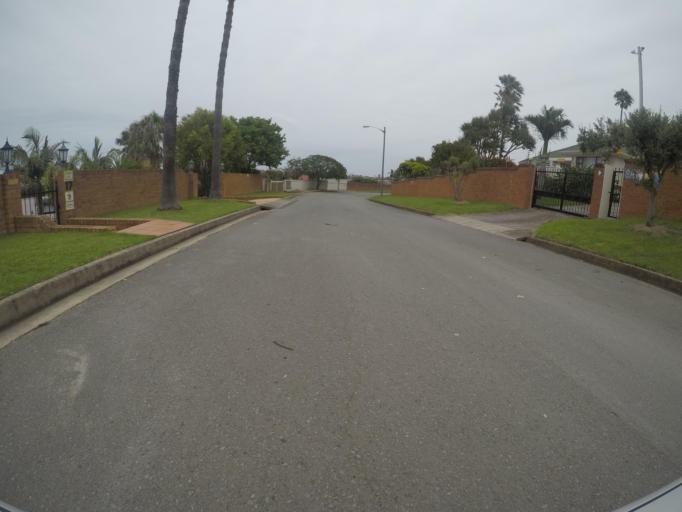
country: ZA
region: Eastern Cape
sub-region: Buffalo City Metropolitan Municipality
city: East London
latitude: -32.9777
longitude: 27.9376
